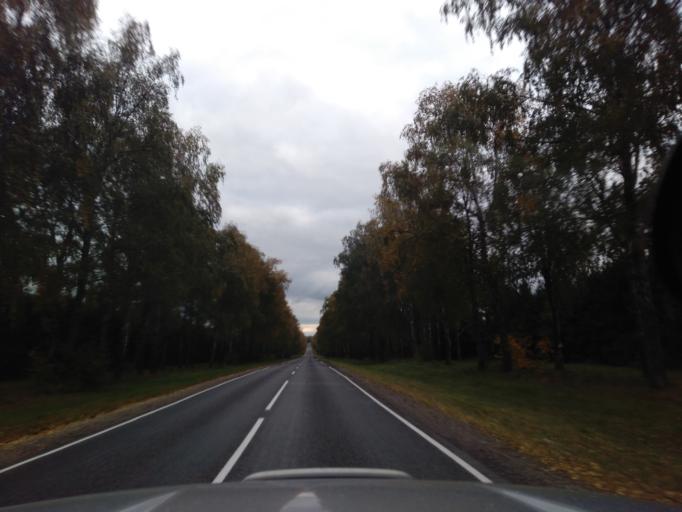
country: BY
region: Minsk
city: Slutsk
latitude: 53.2202
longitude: 27.4696
